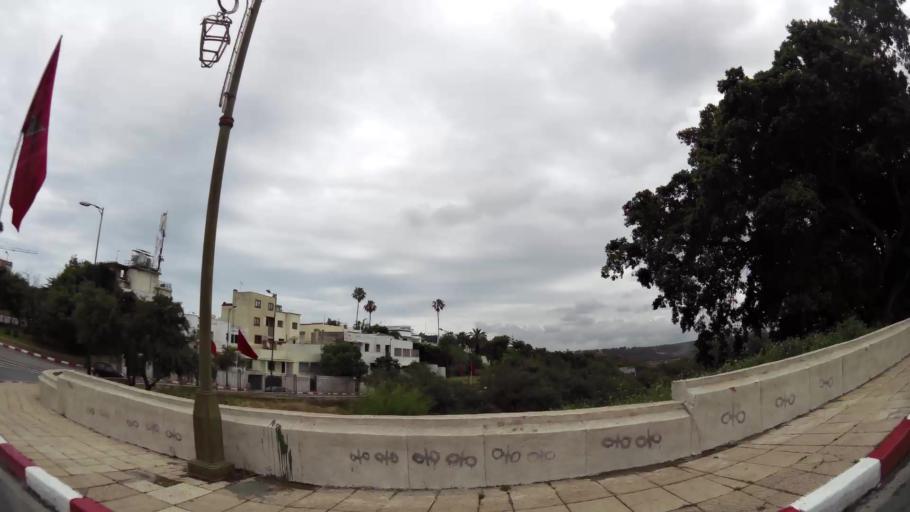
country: MA
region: Rabat-Sale-Zemmour-Zaer
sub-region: Rabat
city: Rabat
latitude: 34.0169
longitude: -6.8227
